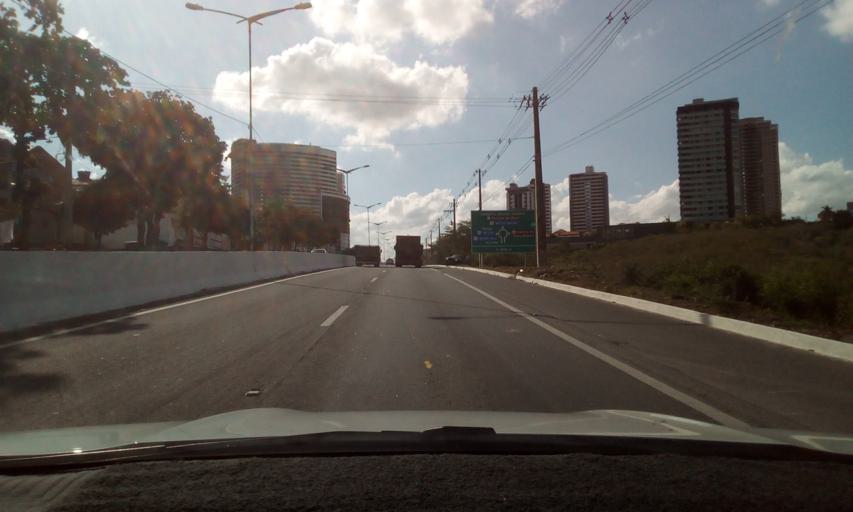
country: BR
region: Paraiba
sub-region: Campina Grande
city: Campina Grande
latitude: -7.2396
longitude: -35.8625
